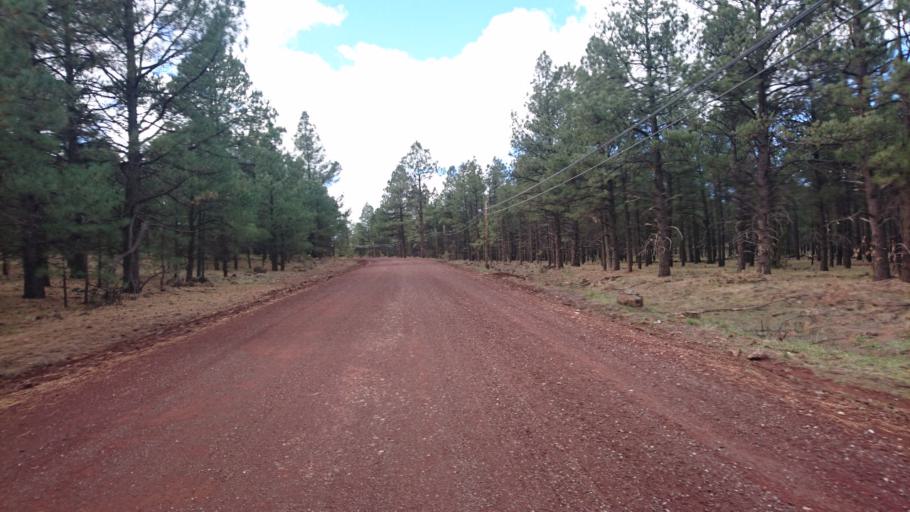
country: US
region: Arizona
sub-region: Coconino County
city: Williams
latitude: 35.2651
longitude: -112.0856
